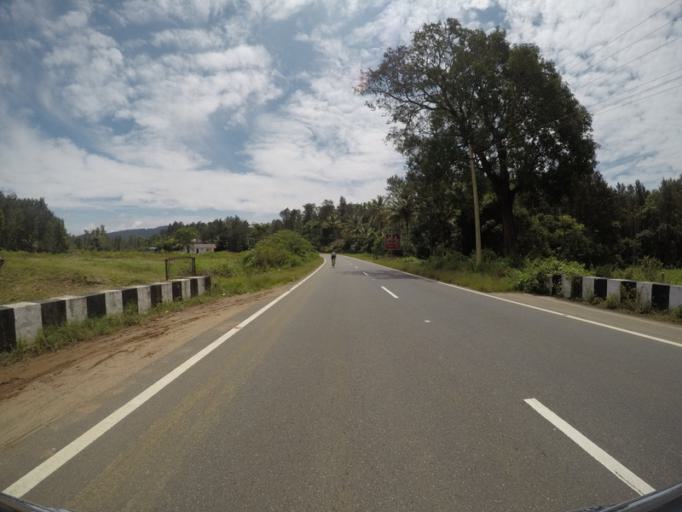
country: IN
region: Karnataka
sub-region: Kodagu
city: Suntikoppa
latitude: 12.4398
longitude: 75.8636
